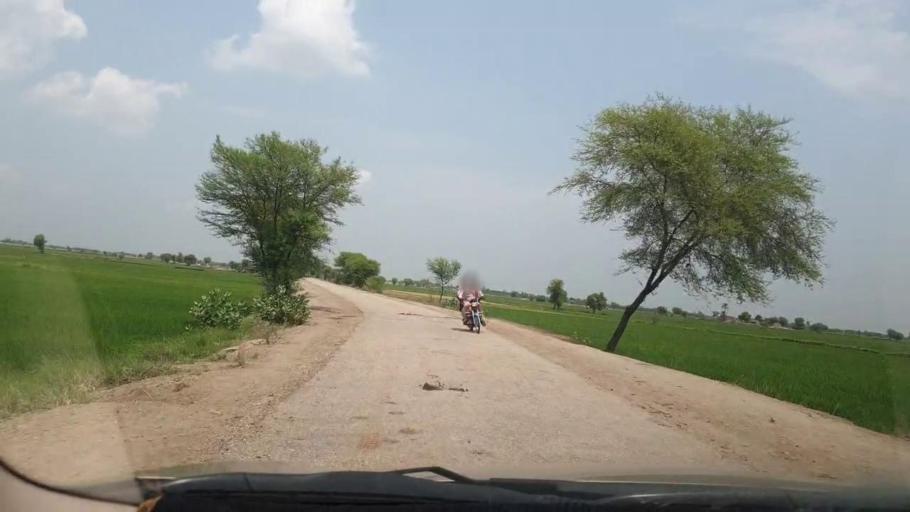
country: PK
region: Sindh
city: Larkana
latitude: 27.6016
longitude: 68.1425
